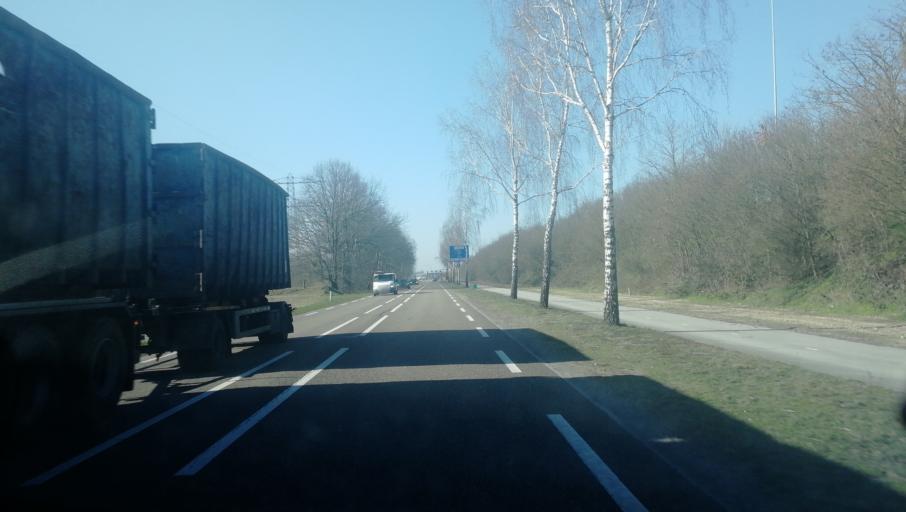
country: NL
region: Limburg
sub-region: Gemeente Venlo
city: Tegelen
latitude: 51.3893
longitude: 6.1020
